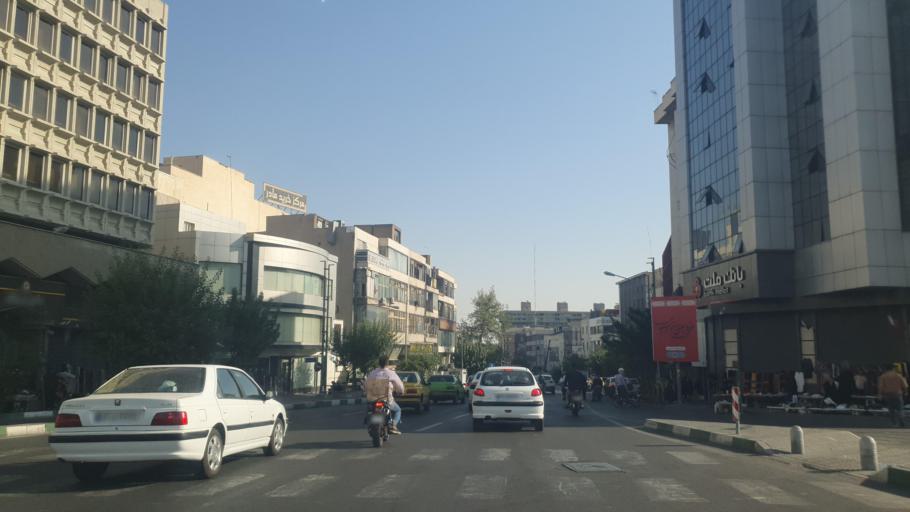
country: IR
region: Tehran
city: Tehran
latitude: 35.7154
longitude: 51.4261
